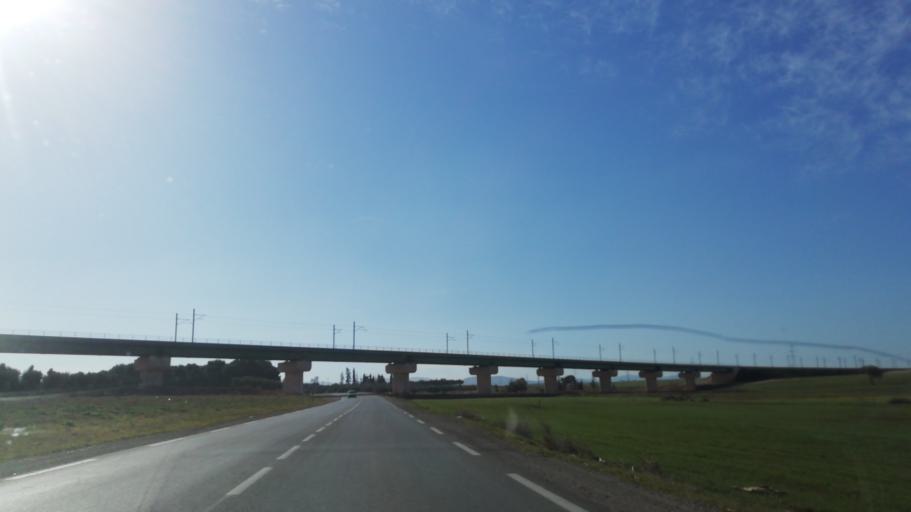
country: DZ
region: Tlemcen
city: Ouled Mimoun
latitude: 35.0084
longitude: -0.9064
